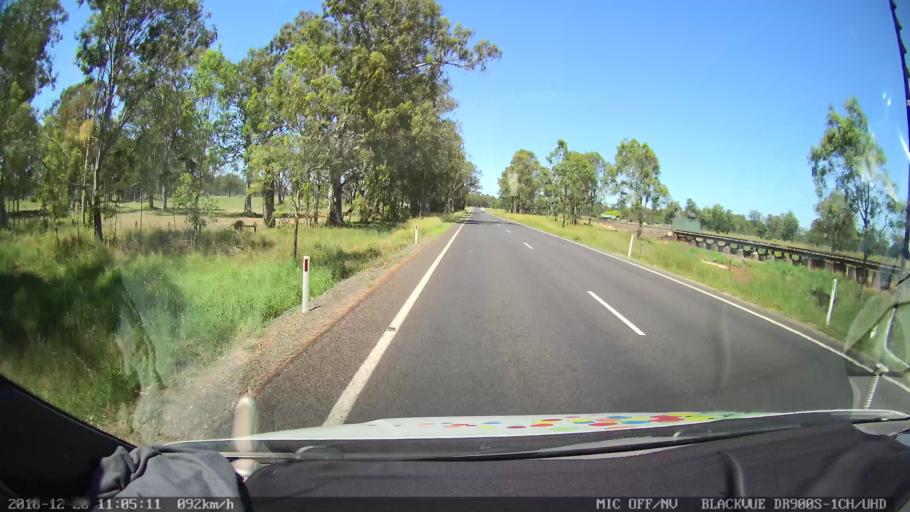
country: AU
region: New South Wales
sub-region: Richmond Valley
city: Casino
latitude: -28.8935
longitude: 153.0427
